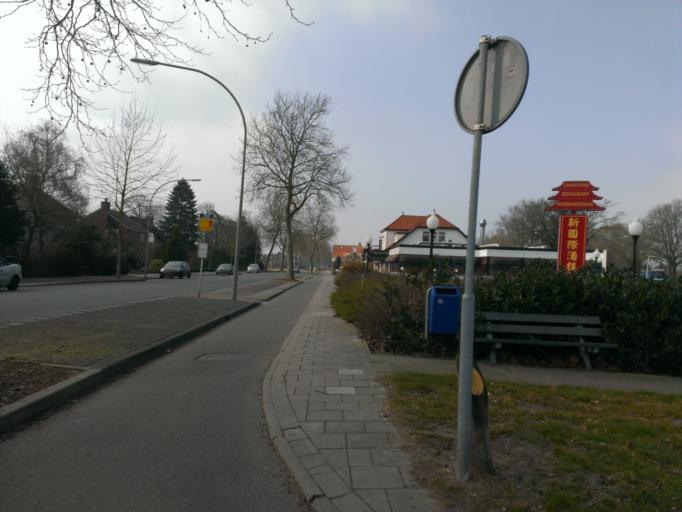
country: NL
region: Overijssel
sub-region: Gemeente Almelo
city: Almelo
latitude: 52.3449
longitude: 6.6827
